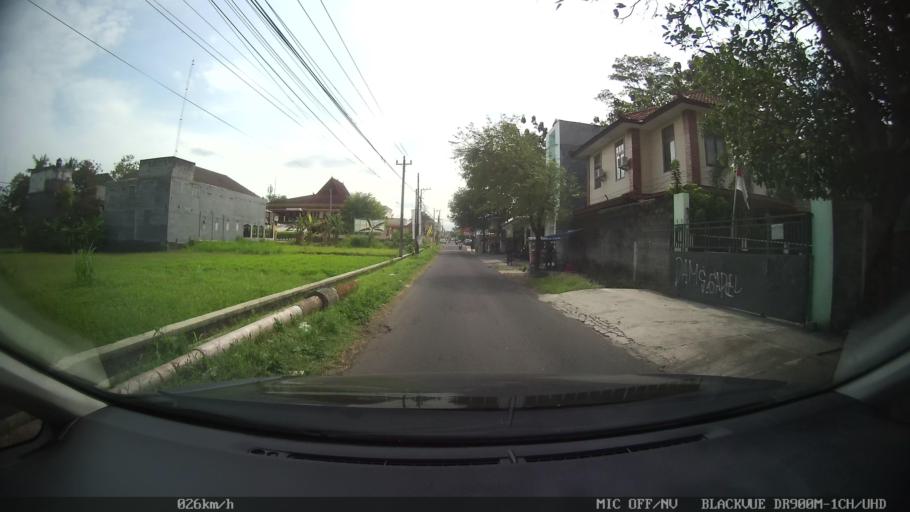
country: ID
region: Daerah Istimewa Yogyakarta
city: Depok
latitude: -7.7602
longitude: 110.4272
